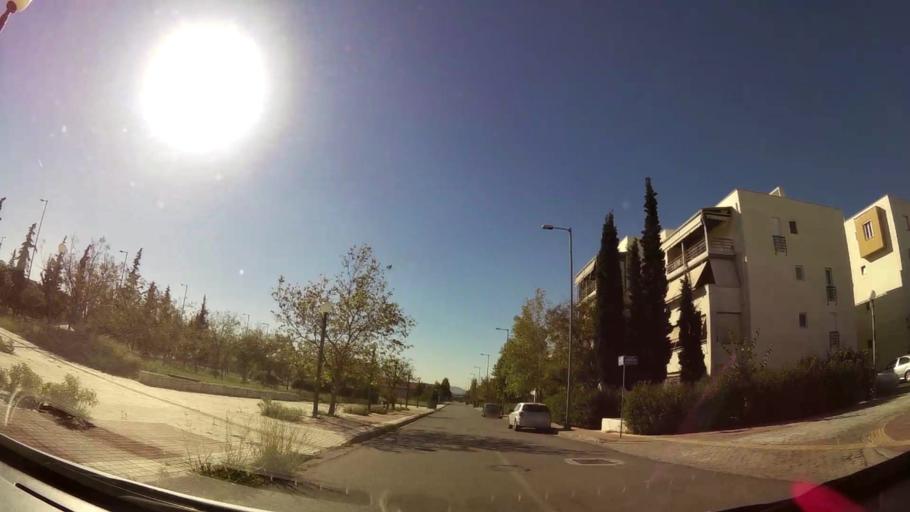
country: GR
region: Attica
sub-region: Nomarchia Anatolikis Attikis
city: Thrakomakedones
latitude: 38.1067
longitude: 23.7673
